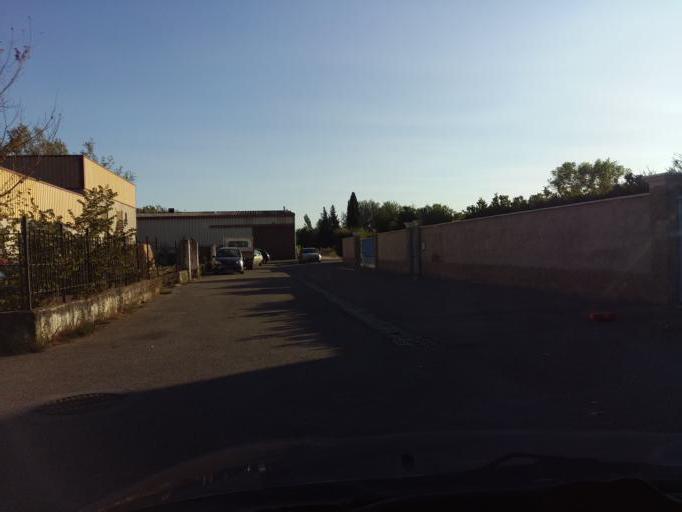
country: FR
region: Provence-Alpes-Cote d'Azur
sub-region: Departement du Vaucluse
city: Loriol-du-Comtat
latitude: 44.0787
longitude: 4.9916
